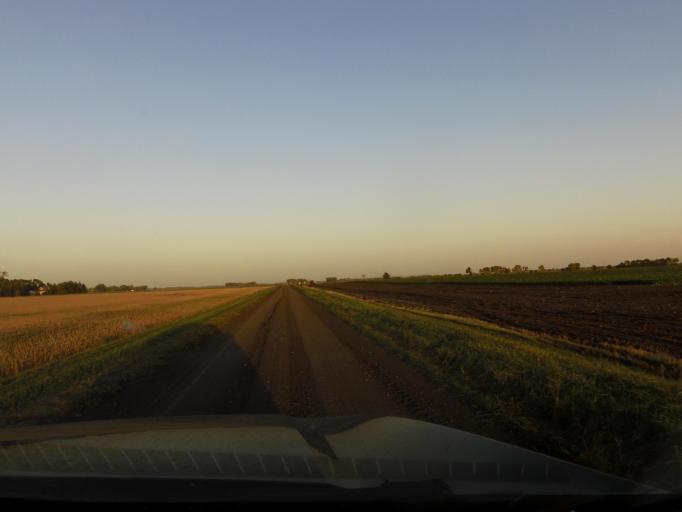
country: US
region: North Dakota
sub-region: Walsh County
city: Grafton
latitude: 48.3831
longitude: -97.2298
